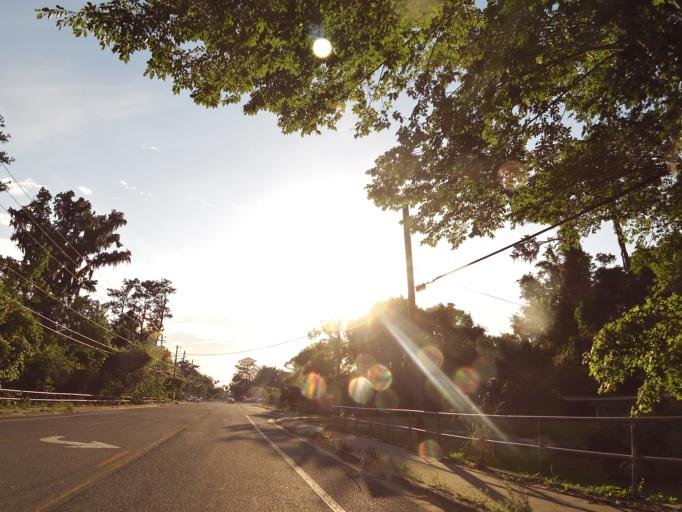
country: US
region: Florida
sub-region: Duval County
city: Jacksonville
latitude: 30.2920
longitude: -81.7285
